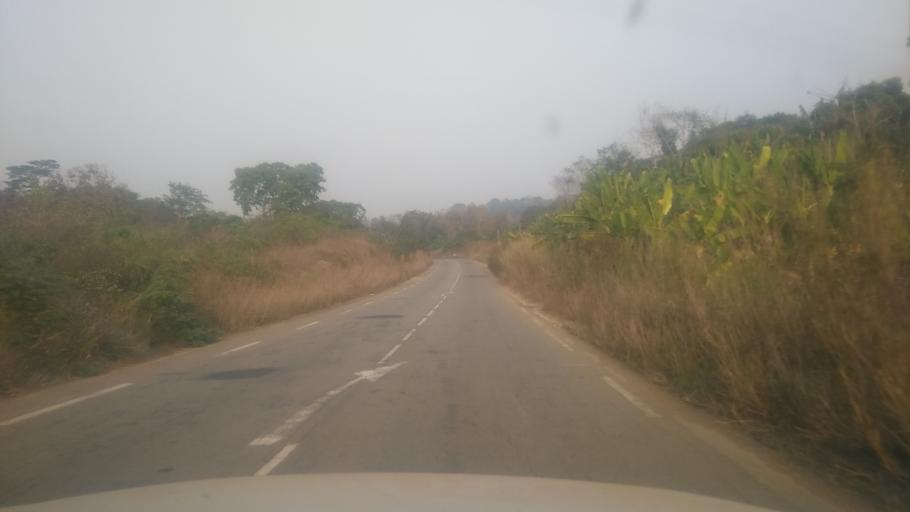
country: CM
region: Centre
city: Bafia
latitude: 4.8345
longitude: 11.0622
